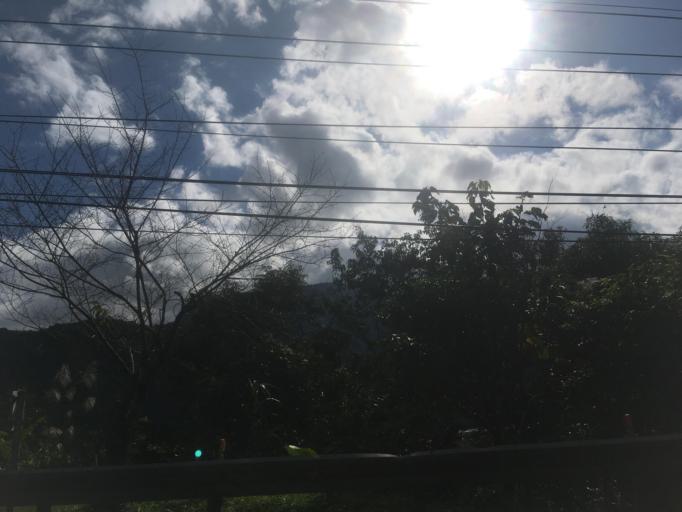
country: TW
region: Taiwan
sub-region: Yilan
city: Yilan
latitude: 24.6239
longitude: 121.5376
